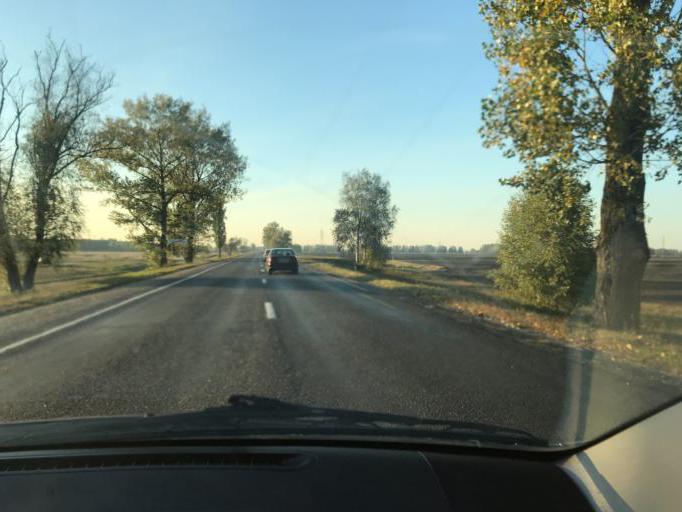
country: BY
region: Brest
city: Pinsk
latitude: 52.0669
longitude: 26.1887
